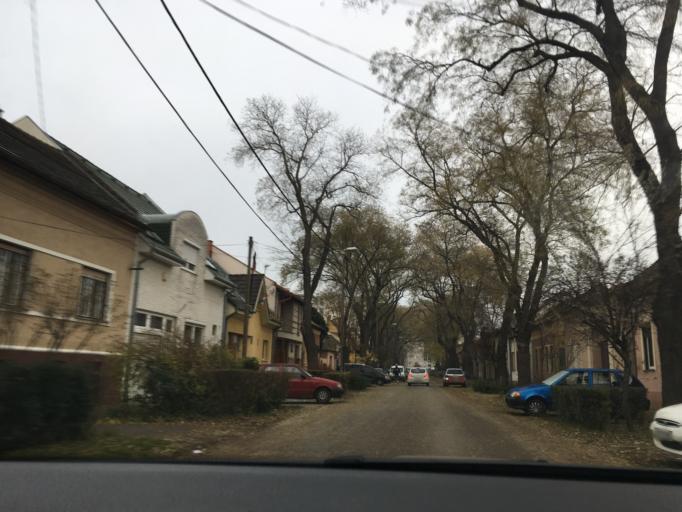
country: HU
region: Hajdu-Bihar
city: Debrecen
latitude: 47.5345
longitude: 21.6385
